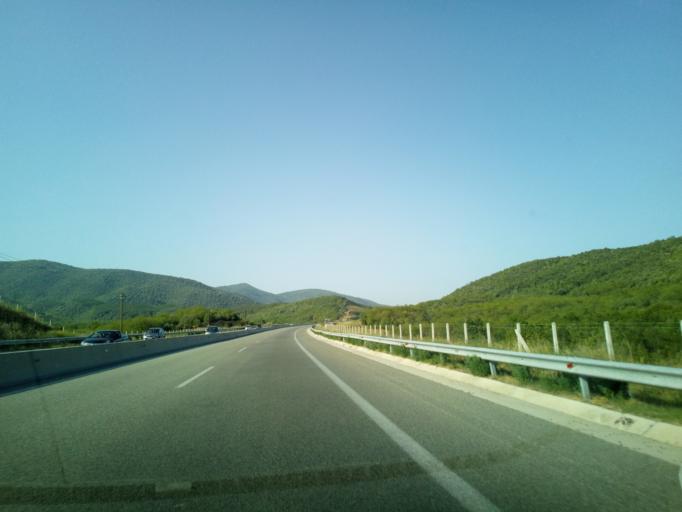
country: GR
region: Central Macedonia
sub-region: Nomos Thessalonikis
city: Nea Vrasna
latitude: 40.6864
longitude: 23.6223
